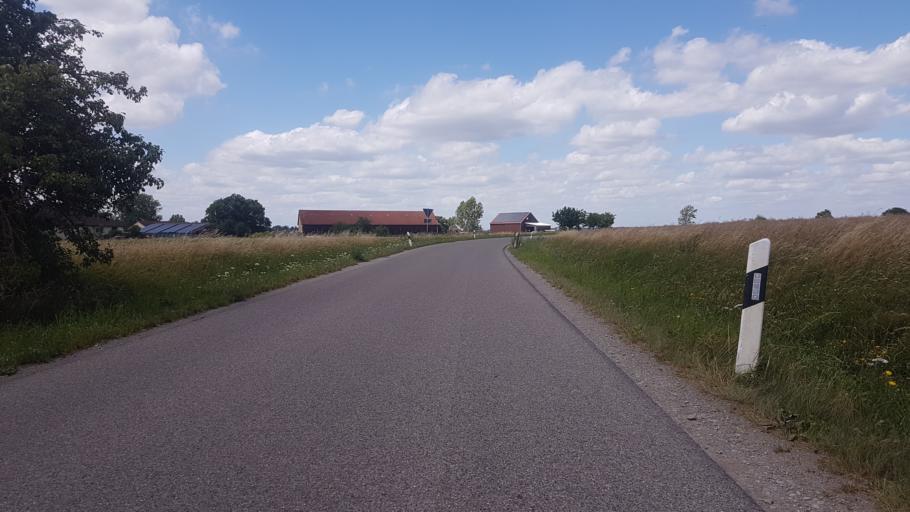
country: DE
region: Bavaria
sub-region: Regierungsbezirk Mittelfranken
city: Geslau
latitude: 49.3322
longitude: 10.3359
